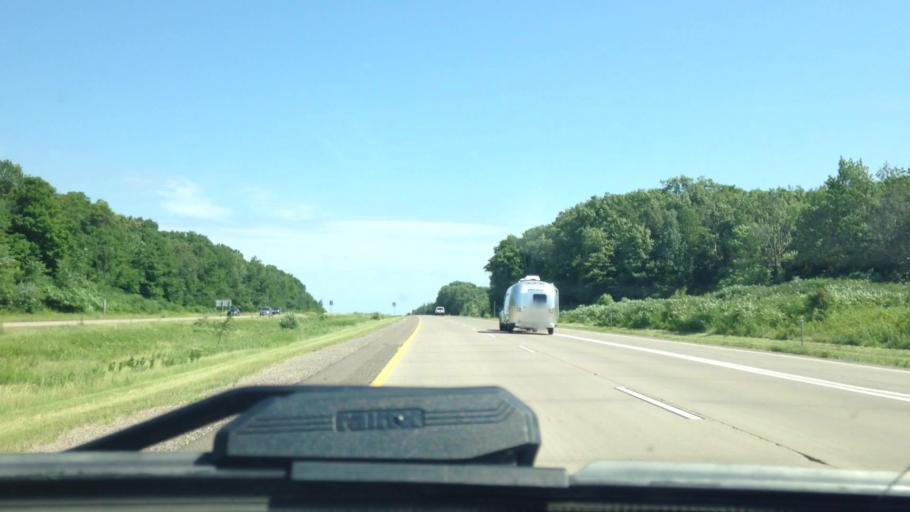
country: US
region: Wisconsin
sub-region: Barron County
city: Rice Lake
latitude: 45.5152
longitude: -91.7603
